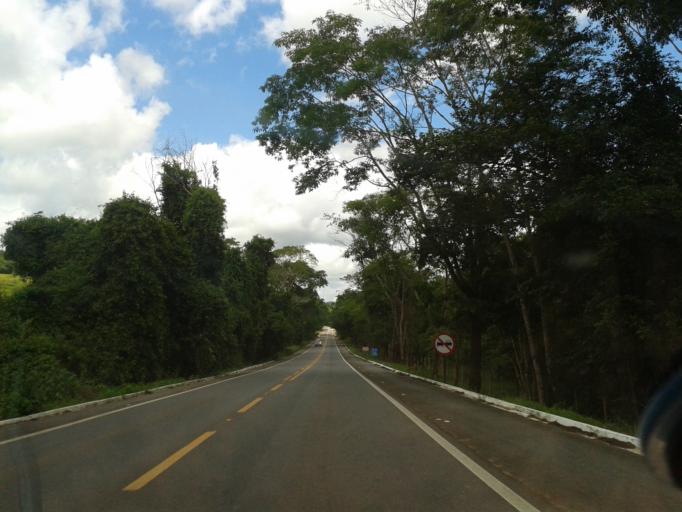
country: BR
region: Goias
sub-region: Goias
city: Goias
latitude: -15.9054
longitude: -50.1177
